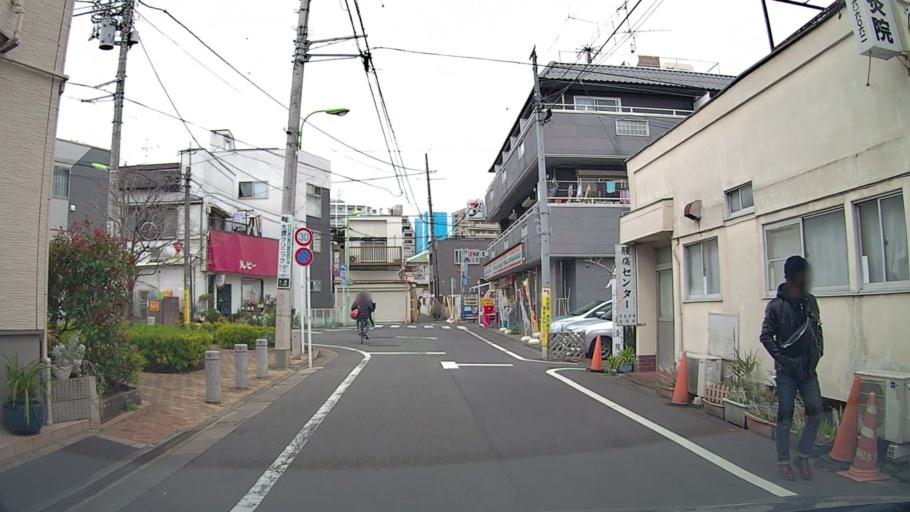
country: JP
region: Tokyo
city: Tokyo
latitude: 35.6711
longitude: 139.6661
